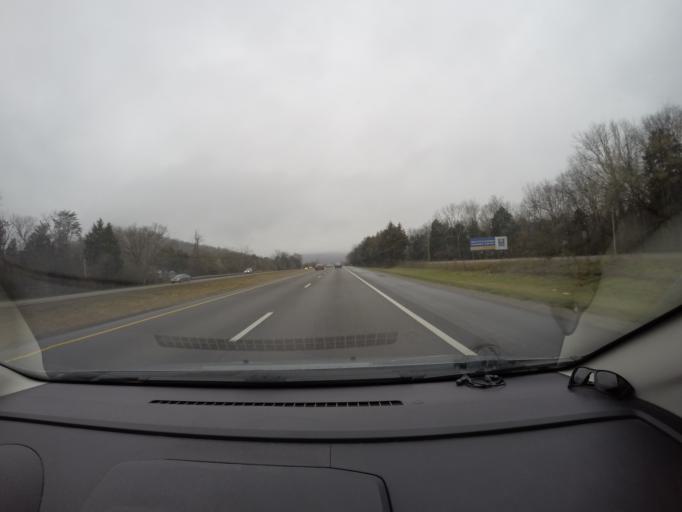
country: US
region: Tennessee
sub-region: Marion County
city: Kimball
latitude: 35.0815
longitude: -85.7367
